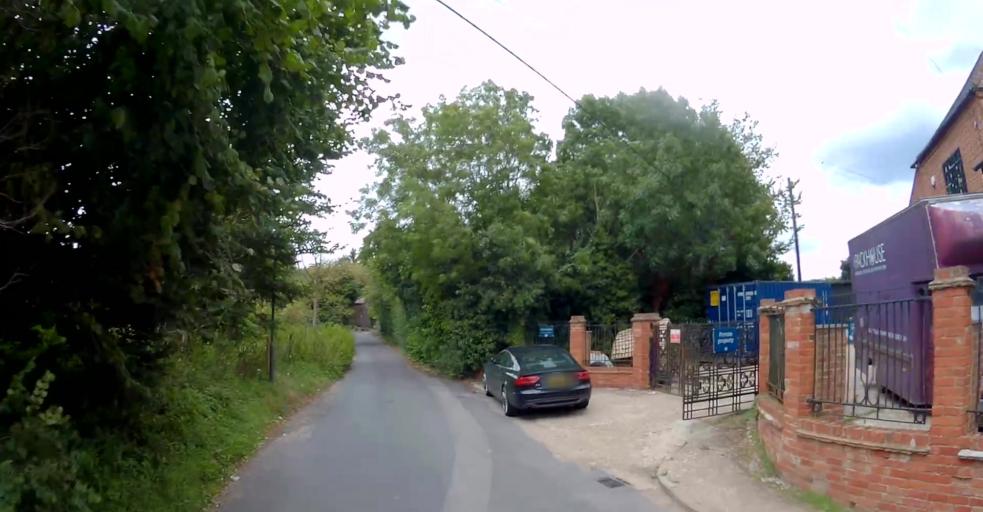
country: GB
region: England
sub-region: Hampshire
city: Aldershot
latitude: 51.2237
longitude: -0.7542
